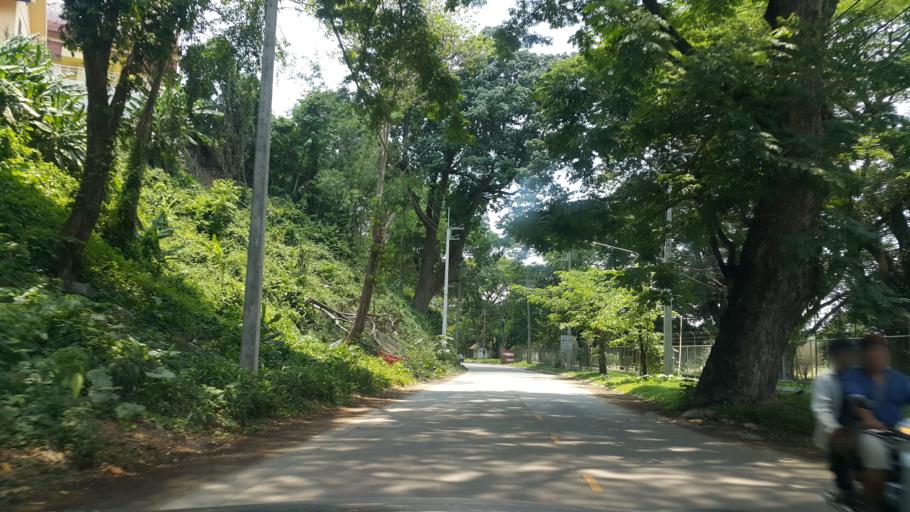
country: TH
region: Chiang Rai
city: Chiang Rai
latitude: 19.9163
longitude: 99.8226
